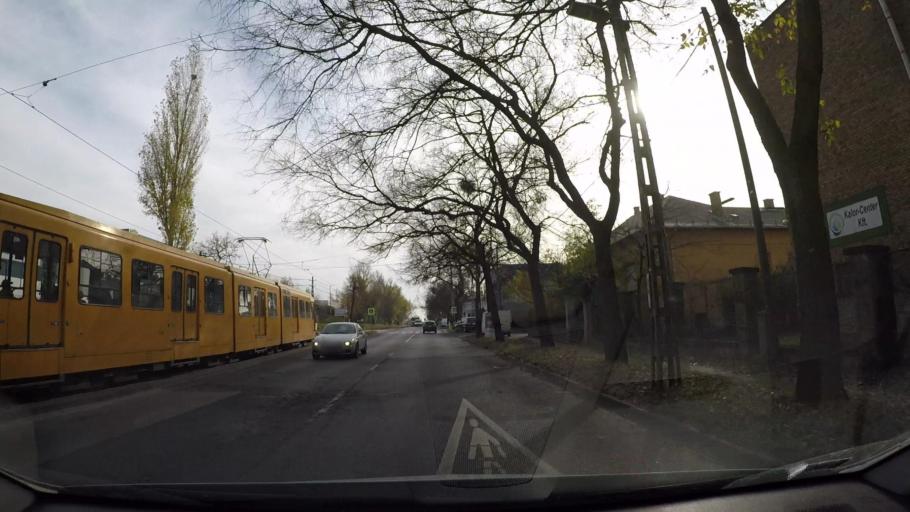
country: HU
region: Budapest
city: Budapest X. keruelet
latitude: 47.4814
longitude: 19.1602
